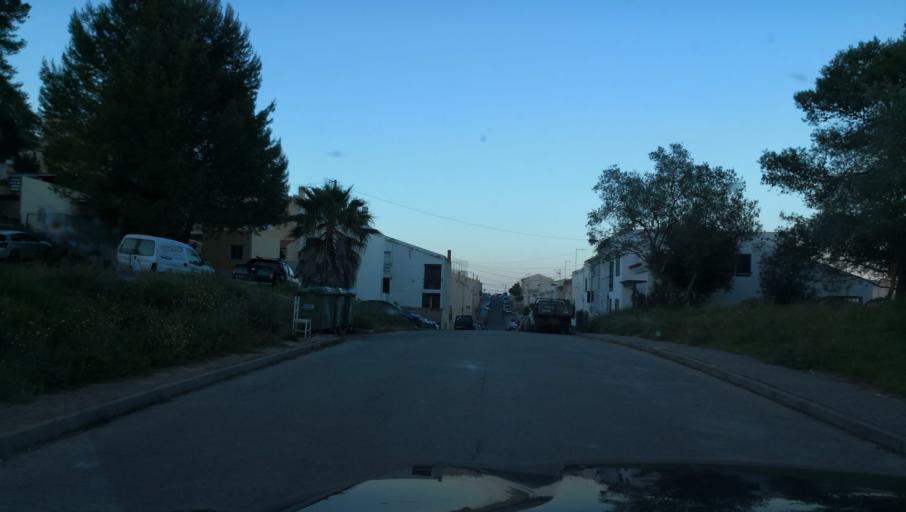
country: PT
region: Setubal
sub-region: Setubal
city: Setubal
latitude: 38.5240
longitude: -8.9144
